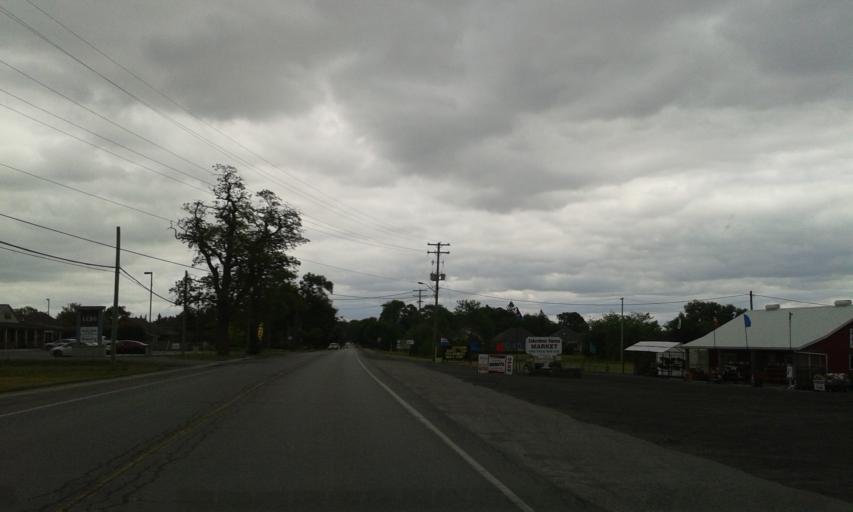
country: CA
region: Ontario
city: Prince Edward
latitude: 43.9485
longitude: -77.3662
